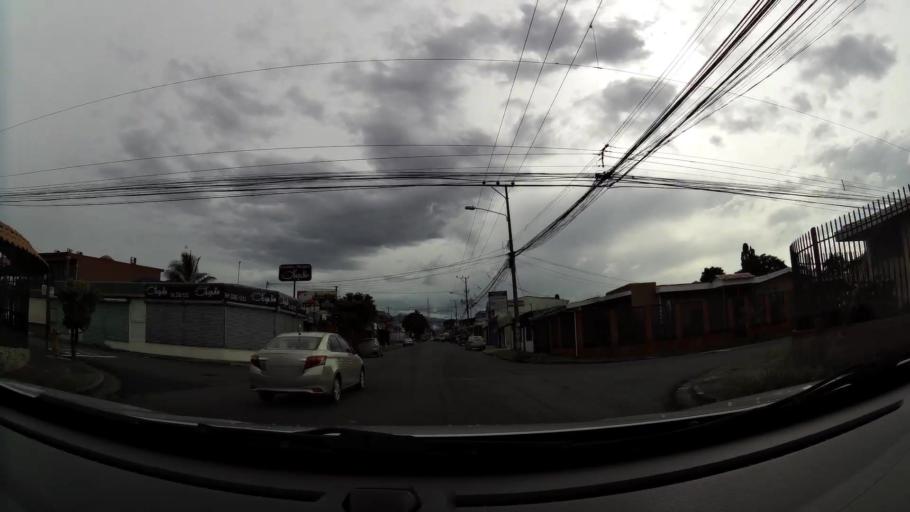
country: CR
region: San Jose
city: San Juan
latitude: 9.9625
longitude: -84.0846
